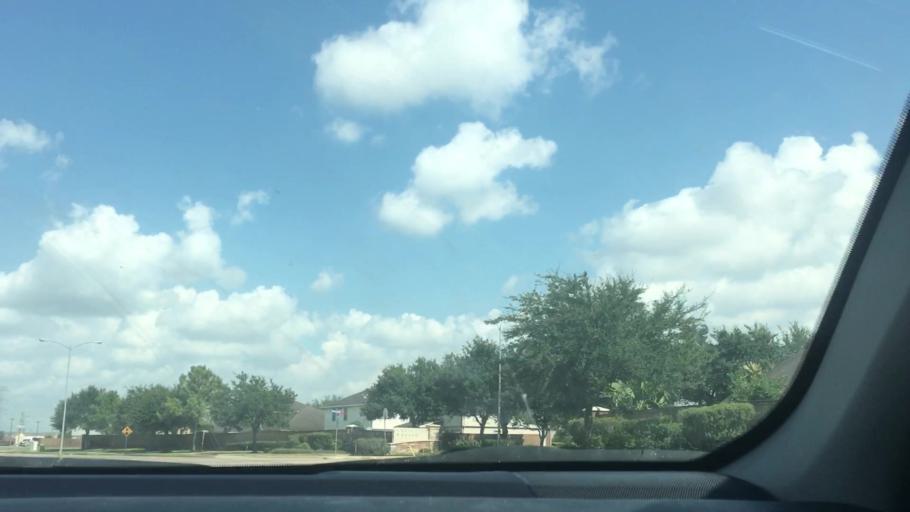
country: US
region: Texas
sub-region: Fort Bend County
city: Fifth Street
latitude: 29.6000
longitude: -95.5621
